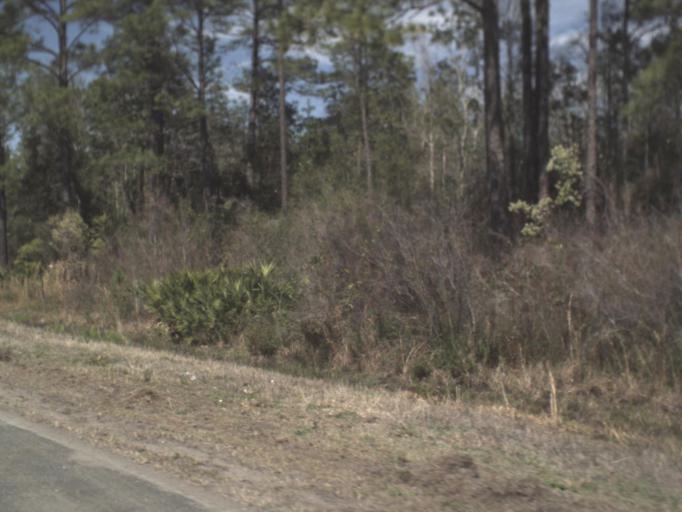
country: US
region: Florida
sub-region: Wakulla County
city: Crawfordville
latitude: 30.3084
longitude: -84.4309
